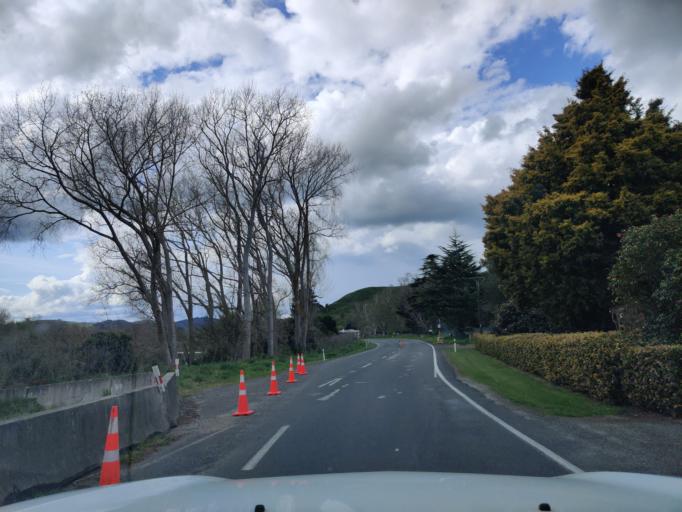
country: NZ
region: Manawatu-Wanganui
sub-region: Wanganui District
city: Wanganui
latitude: -39.8757
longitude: 175.1110
